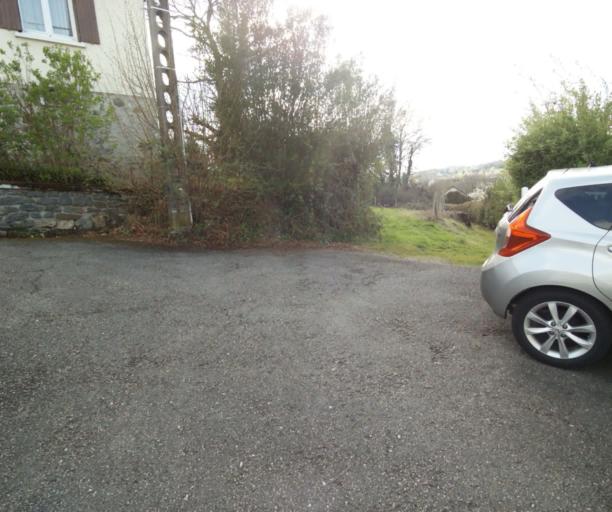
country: FR
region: Limousin
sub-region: Departement de la Correze
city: Tulle
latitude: 45.2552
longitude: 1.7489
